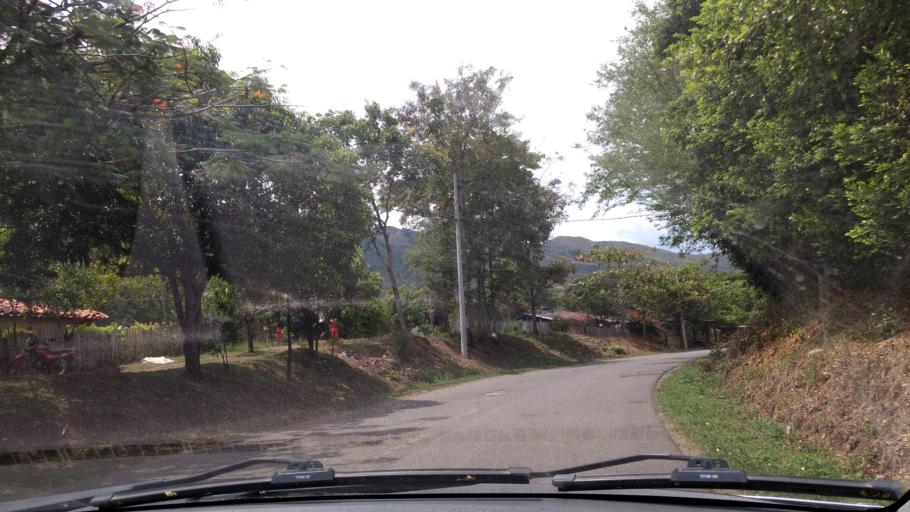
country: CO
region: Cauca
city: Buenos Aires
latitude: 3.0570
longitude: -76.6586
